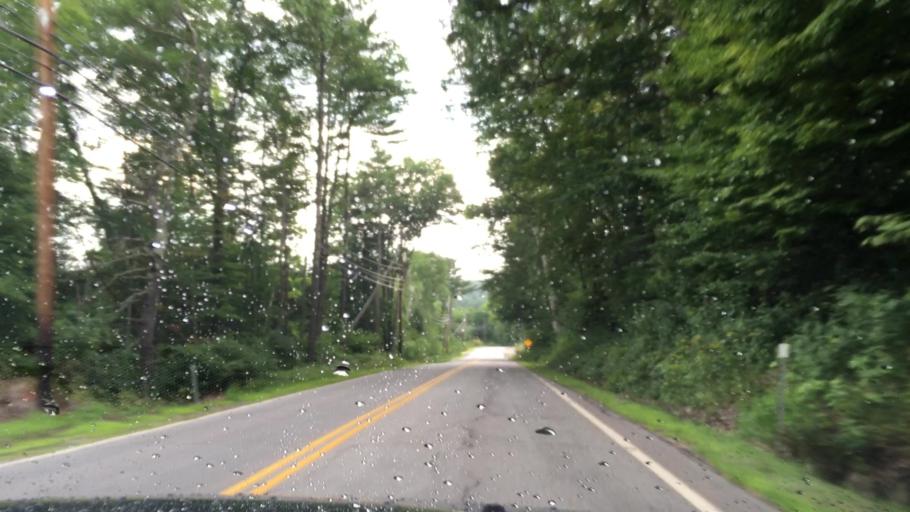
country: US
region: New Hampshire
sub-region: Belknap County
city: Meredith
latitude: 43.6890
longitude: -71.5096
